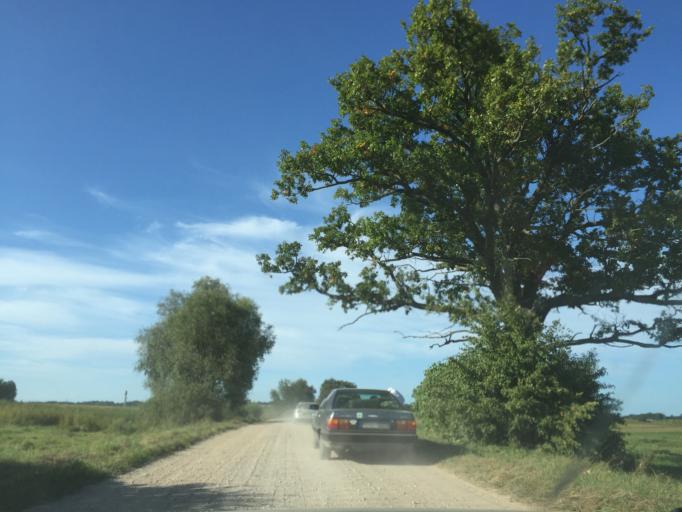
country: LT
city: Zarasai
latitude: 55.8010
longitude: 25.9484
